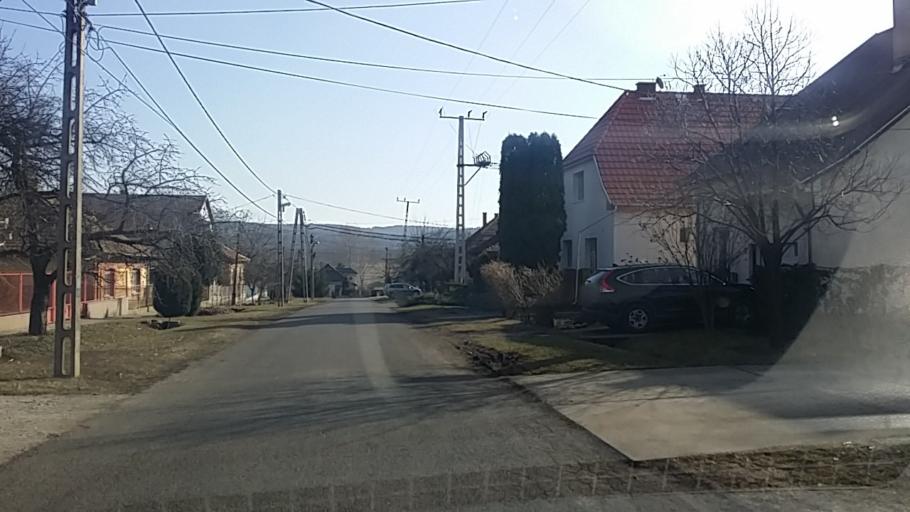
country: HU
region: Heves
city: Gyongyossolymos
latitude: 47.8152
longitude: 19.9376
